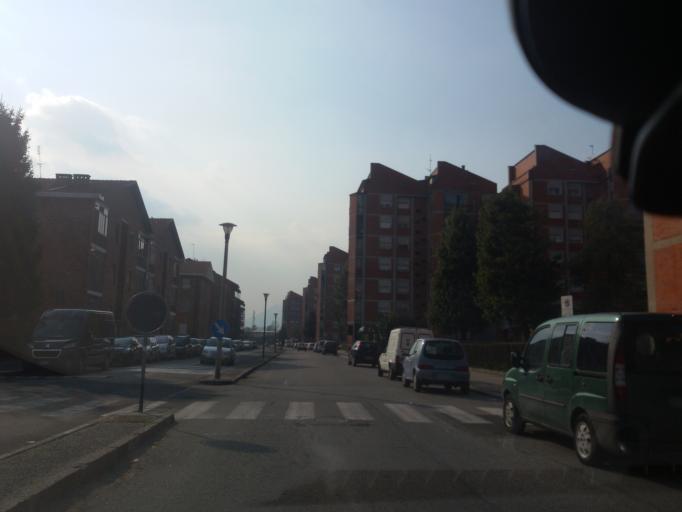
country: IT
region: Piedmont
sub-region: Provincia di Torino
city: Savonera
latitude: 45.1059
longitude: 7.6293
